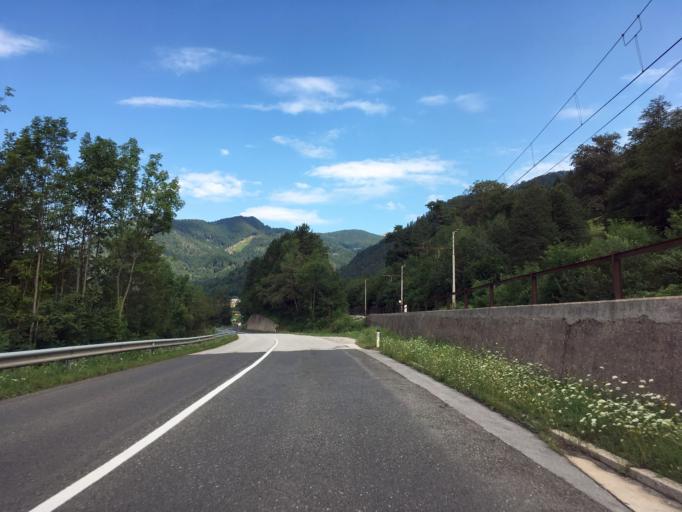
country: SI
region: Jesenice
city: Slovenski Javornik
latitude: 46.4183
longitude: 14.1087
